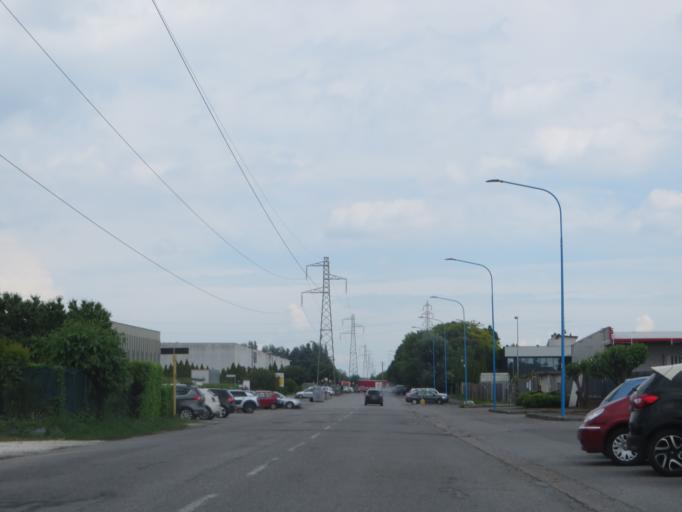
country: IT
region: Lombardy
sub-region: Provincia di Brescia
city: Roncadelle
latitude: 45.5187
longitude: 10.1611
